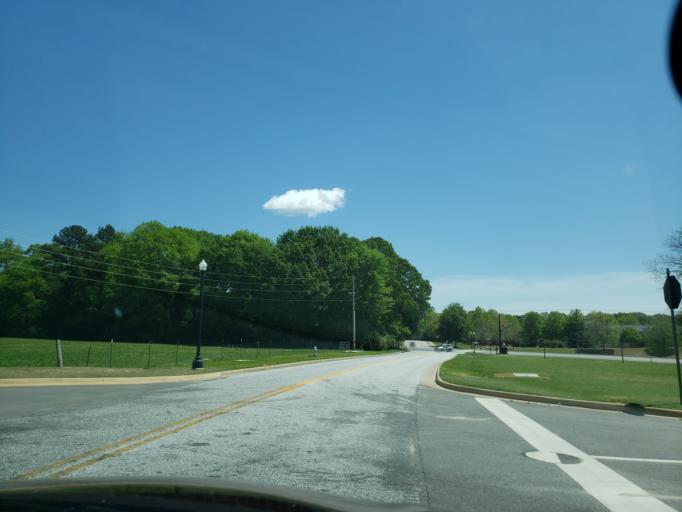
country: US
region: Alabama
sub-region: Lee County
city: Auburn
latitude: 32.5889
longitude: -85.4864
